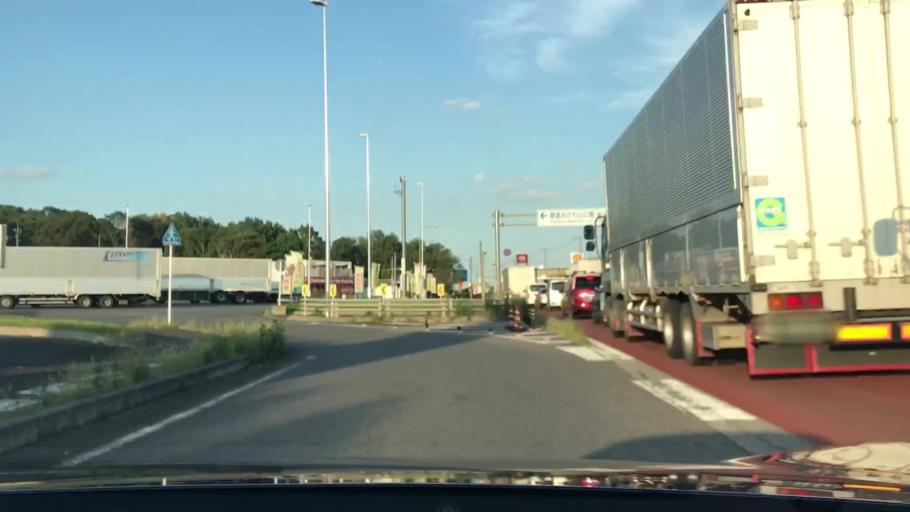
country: JP
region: Tochigi
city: Sano
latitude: 36.2965
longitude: 139.6258
